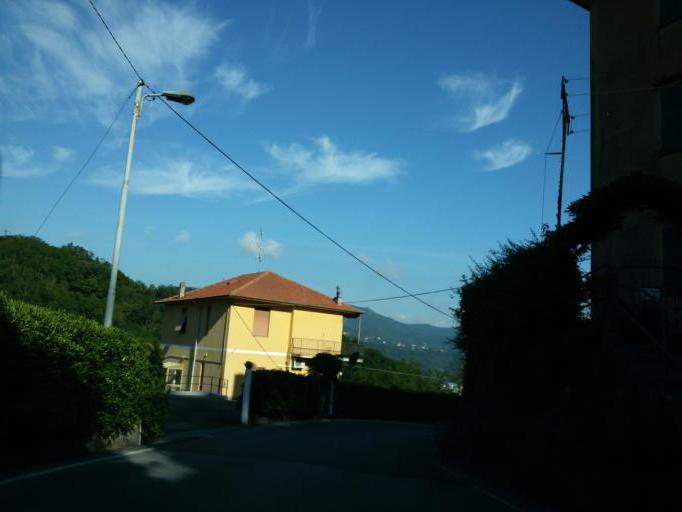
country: IT
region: Liguria
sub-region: Provincia di Genova
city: Santa Marta
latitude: 44.4778
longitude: 8.8858
